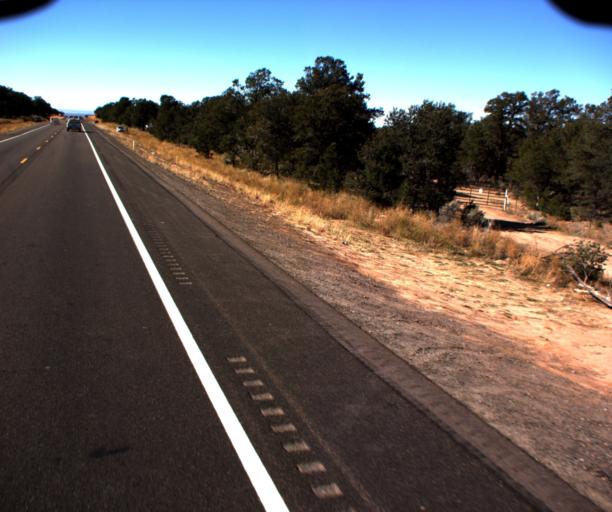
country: US
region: Arizona
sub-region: Apache County
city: Ganado
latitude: 35.7108
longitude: -109.3259
